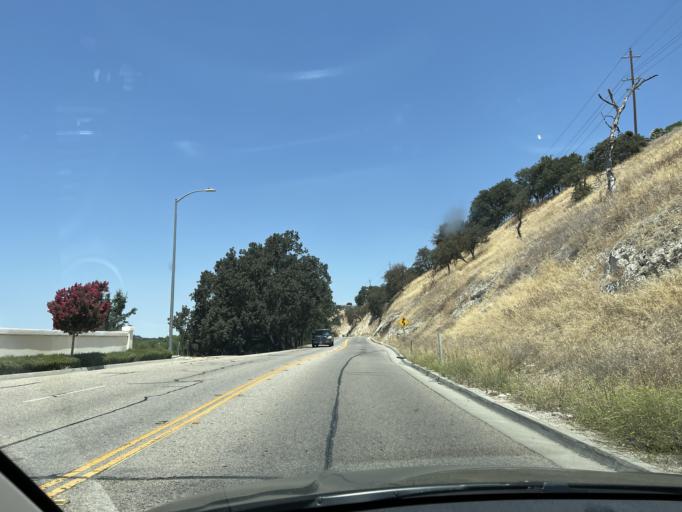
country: US
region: California
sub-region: San Luis Obispo County
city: Paso Robles
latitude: 35.6196
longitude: -120.6802
